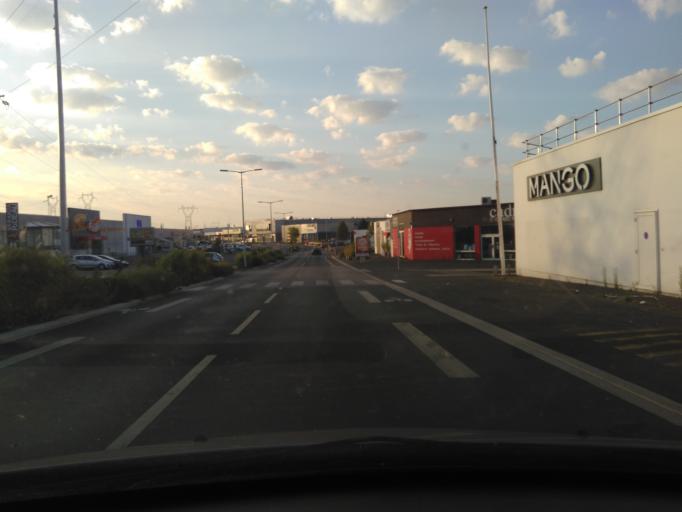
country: FR
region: Poitou-Charentes
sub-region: Departement de la Charente-Maritime
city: Puilboreau
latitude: 46.1772
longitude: -1.1158
